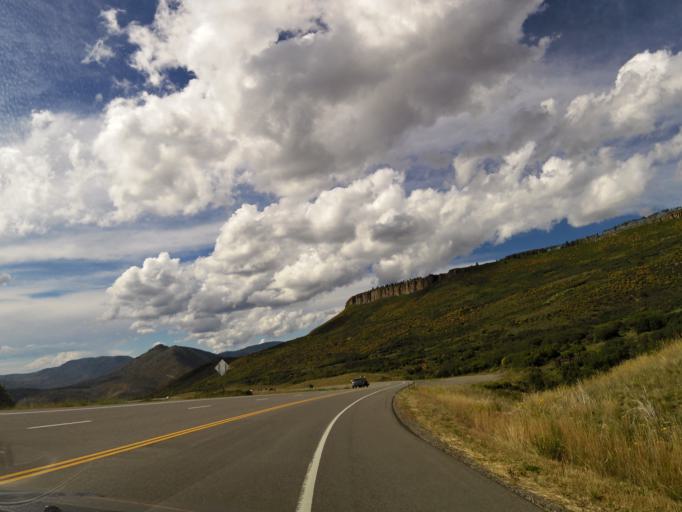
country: US
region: Colorado
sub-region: Hinsdale County
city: Lake City
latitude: 38.3919
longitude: -107.4442
